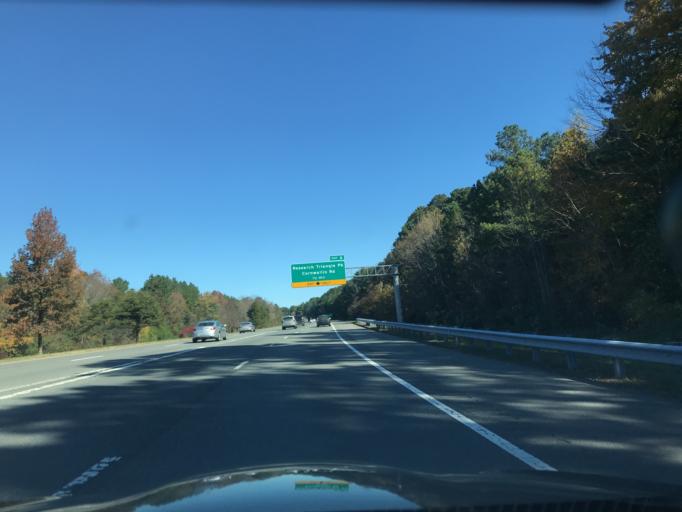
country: US
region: North Carolina
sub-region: Durham County
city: Durham
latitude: 35.9057
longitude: -78.8697
